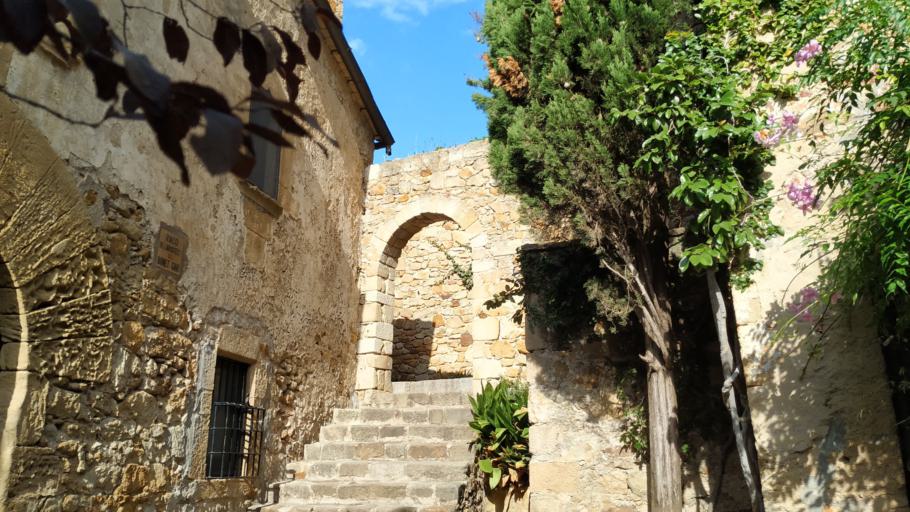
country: ES
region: Catalonia
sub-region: Provincia de Girona
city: Pals
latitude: 41.9727
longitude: 3.1438
